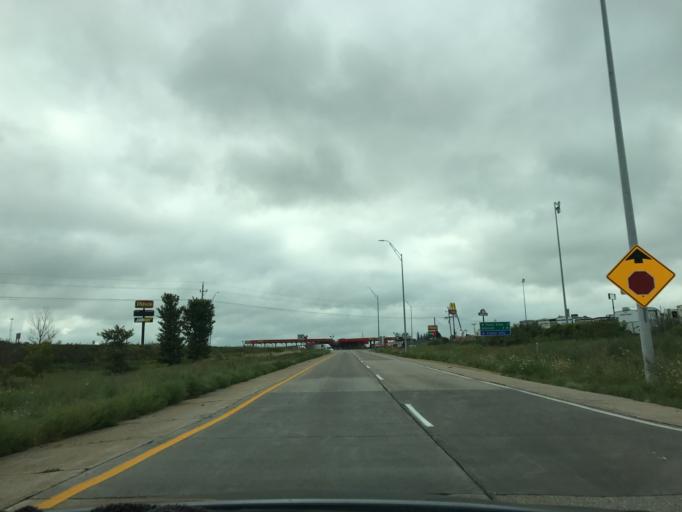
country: US
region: Iowa
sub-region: Scott County
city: Walcott
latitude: 41.6163
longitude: -90.7849
